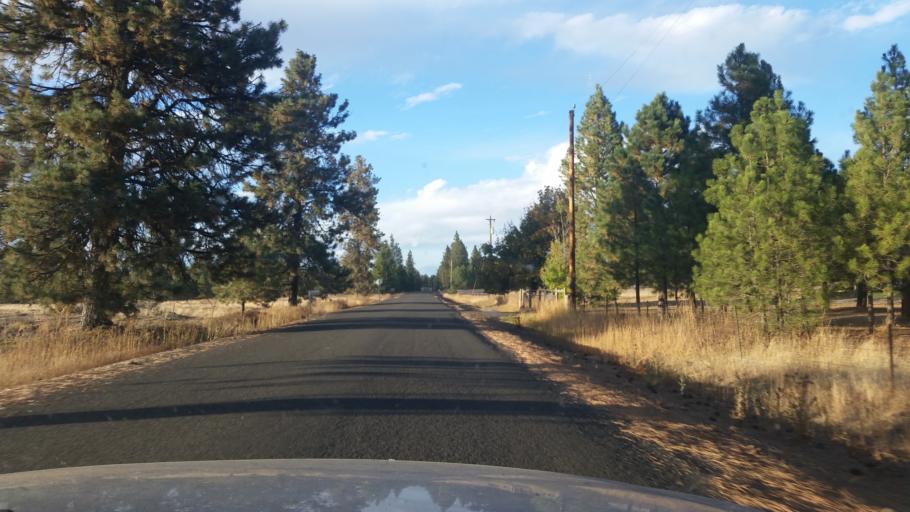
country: US
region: Washington
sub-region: Spokane County
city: Medical Lake
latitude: 47.4390
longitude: -117.7897
